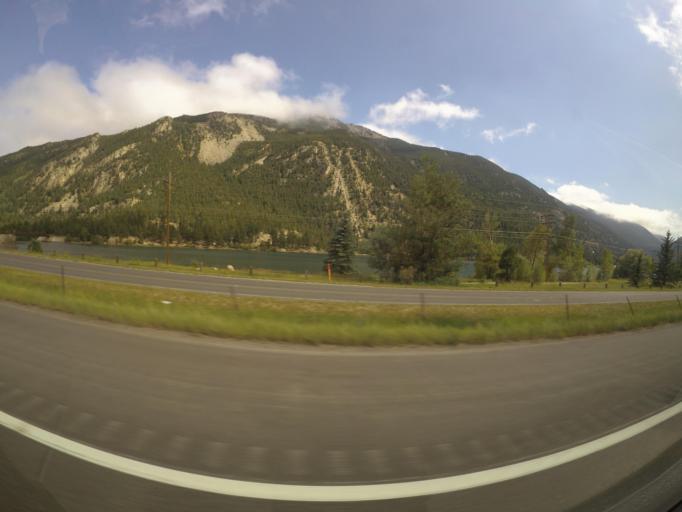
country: US
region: Colorado
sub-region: Clear Creek County
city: Georgetown
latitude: 39.7321
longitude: -105.6927
